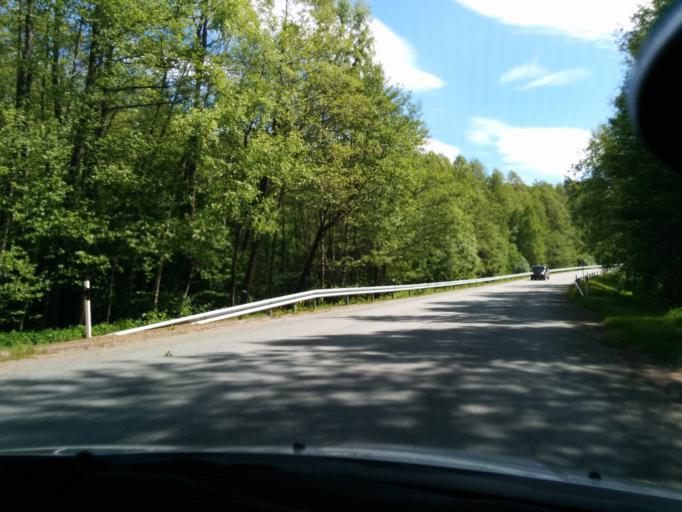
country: EE
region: Harju
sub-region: Loksa linn
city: Loksa
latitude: 59.5591
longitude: 25.9913
